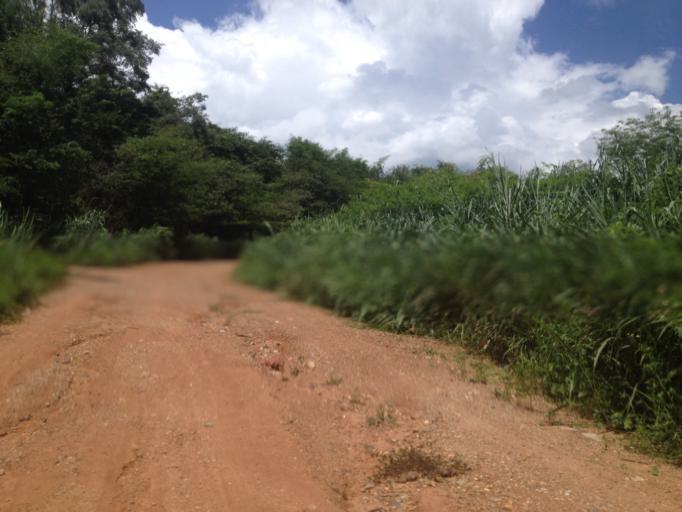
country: TH
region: Chiang Mai
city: Hang Dong
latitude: 18.7533
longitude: 98.9197
